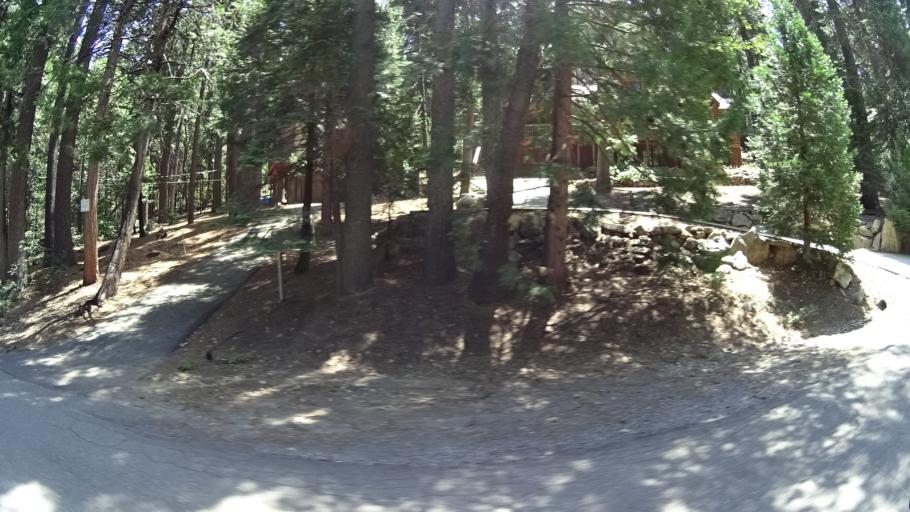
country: US
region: California
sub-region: Calaveras County
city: Arnold
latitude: 38.3069
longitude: -120.2677
